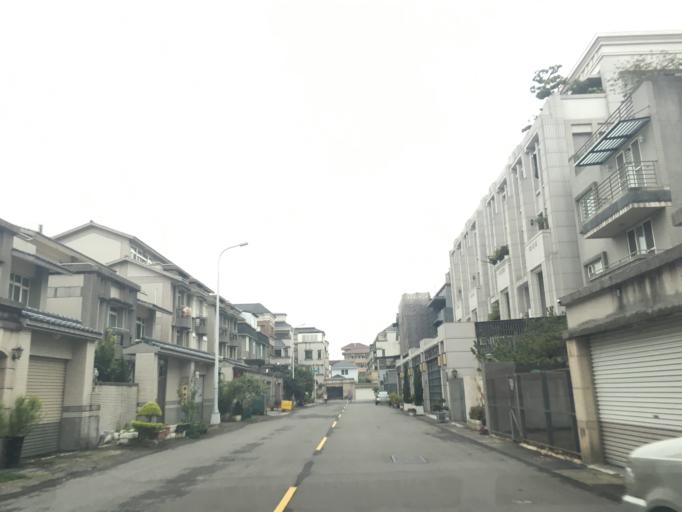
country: TW
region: Taiwan
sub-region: Taichung City
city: Taichung
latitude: 24.1666
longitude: 120.7158
